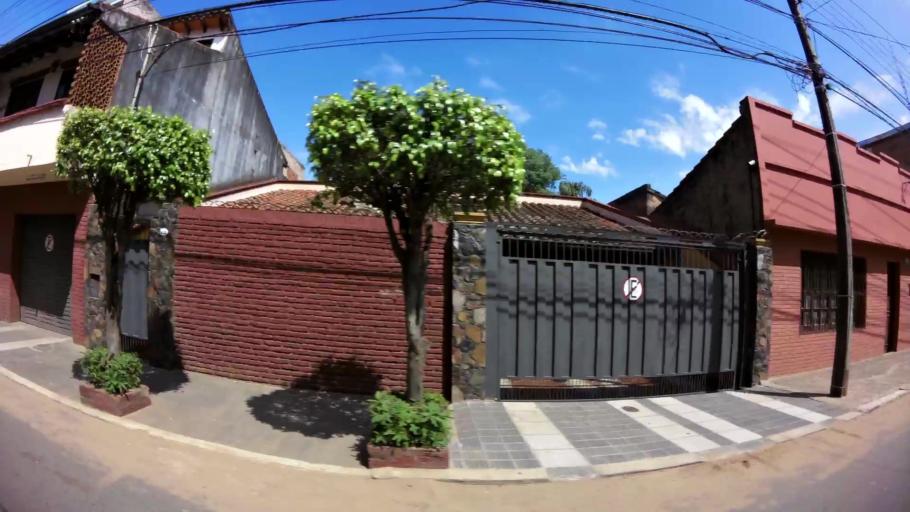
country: PY
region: Central
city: San Lorenzo
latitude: -25.2622
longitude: -57.4910
